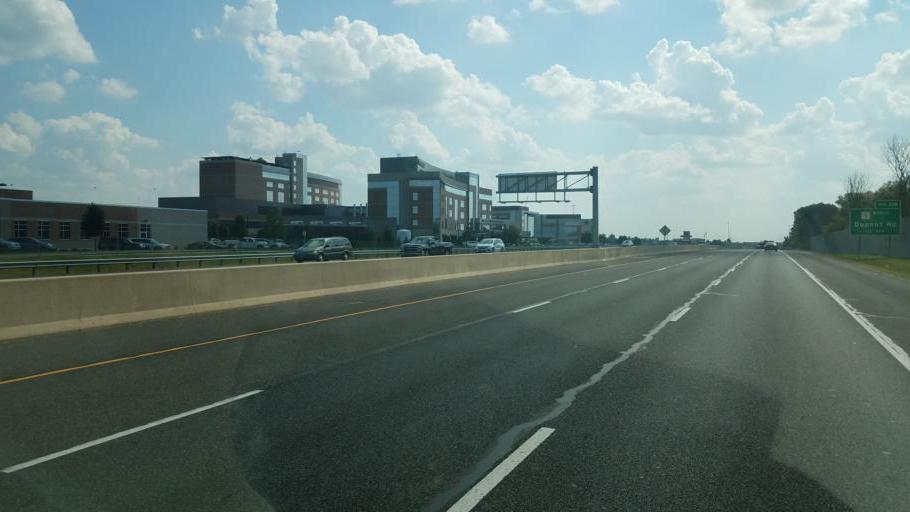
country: US
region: Indiana
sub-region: Allen County
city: Fort Wayne
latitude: 41.1896
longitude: -85.1040
